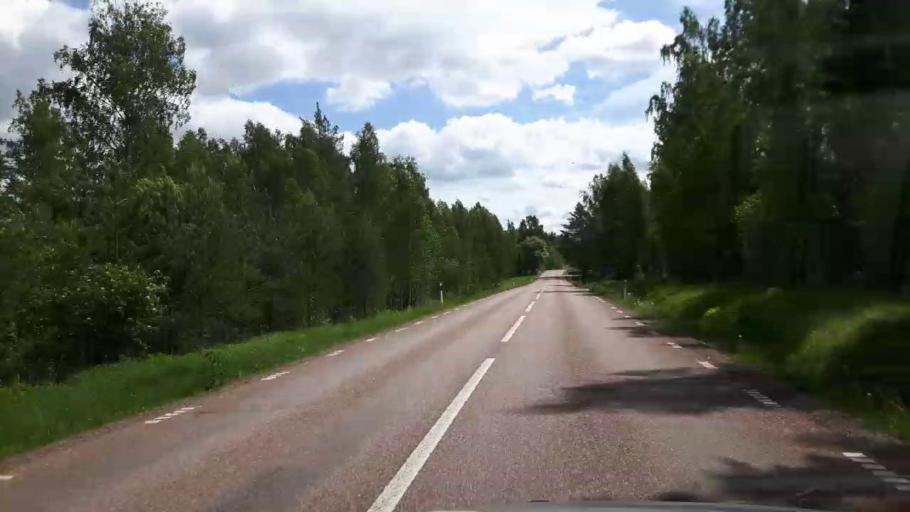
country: SE
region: Dalarna
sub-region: Saters Kommun
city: Saeter
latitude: 60.4124
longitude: 15.8540
